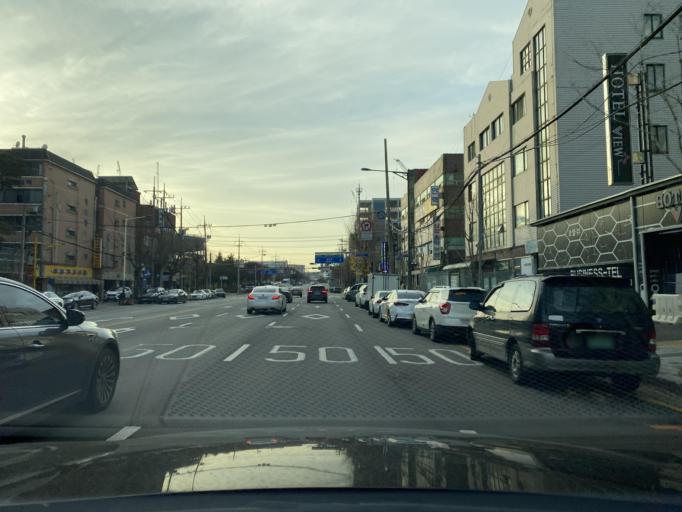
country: KR
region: Incheon
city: Incheon
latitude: 37.5065
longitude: 126.6696
